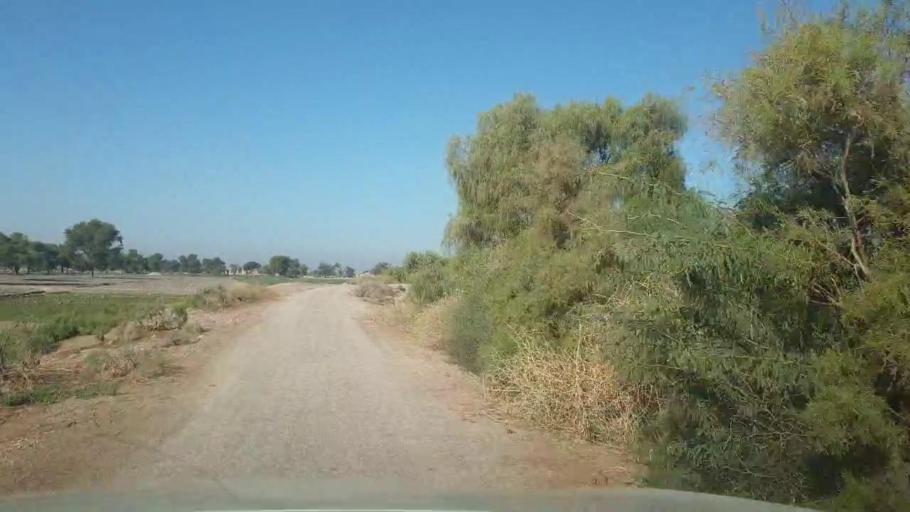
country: PK
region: Sindh
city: Bhan
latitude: 26.5503
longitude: 67.6650
